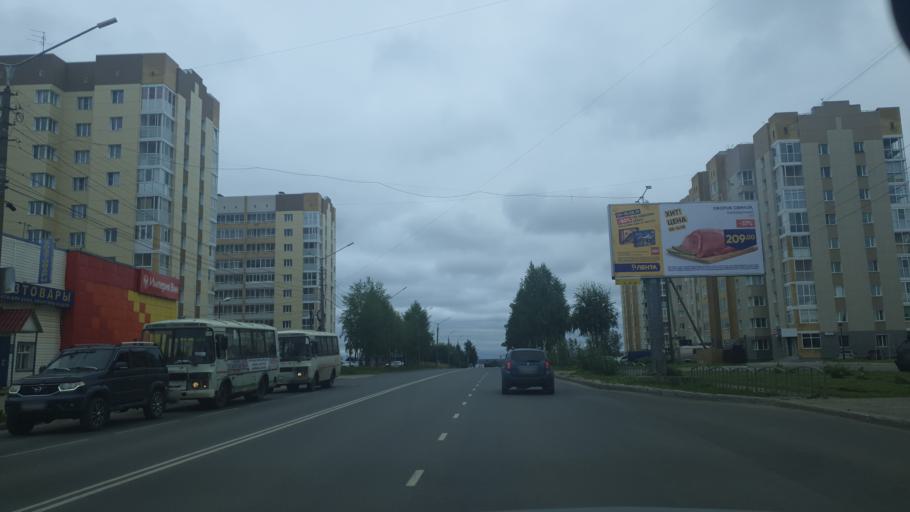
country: RU
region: Komi Republic
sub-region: Syktyvdinskiy Rayon
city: Syktyvkar
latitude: 61.6413
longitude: 50.8101
